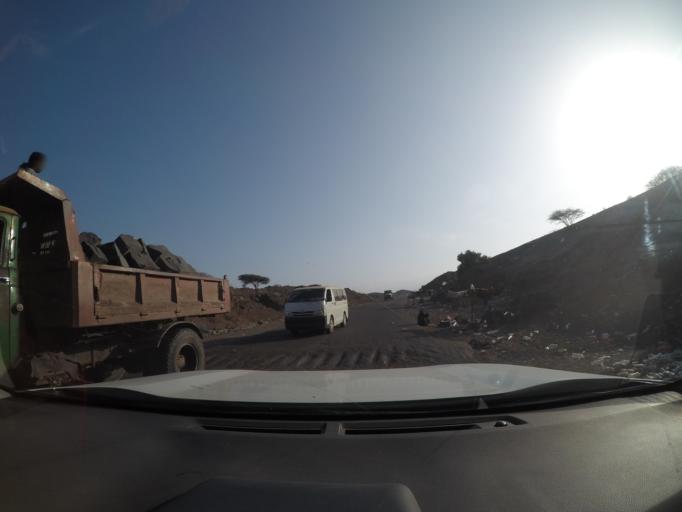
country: YE
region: Lahij
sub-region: Al Milah
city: Al Milah
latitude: 13.3840
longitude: 44.8103
